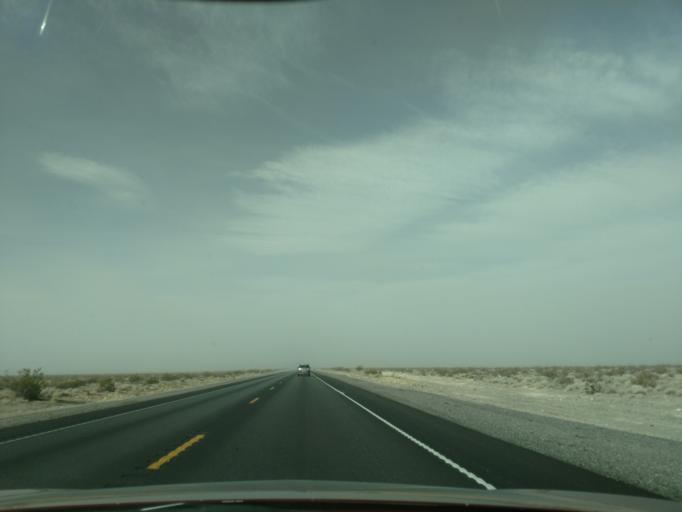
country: US
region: Nevada
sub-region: Nye County
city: Beatty
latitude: 36.6350
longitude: -116.3646
